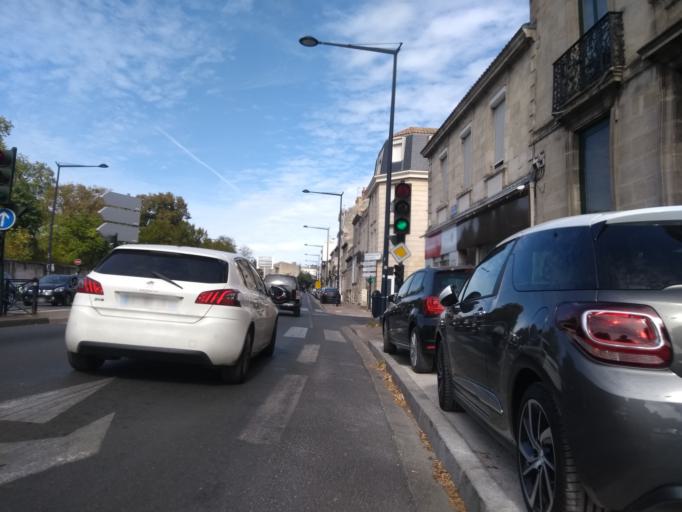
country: FR
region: Aquitaine
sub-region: Departement de la Gironde
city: Bordeaux
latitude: 44.8464
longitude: -0.5982
